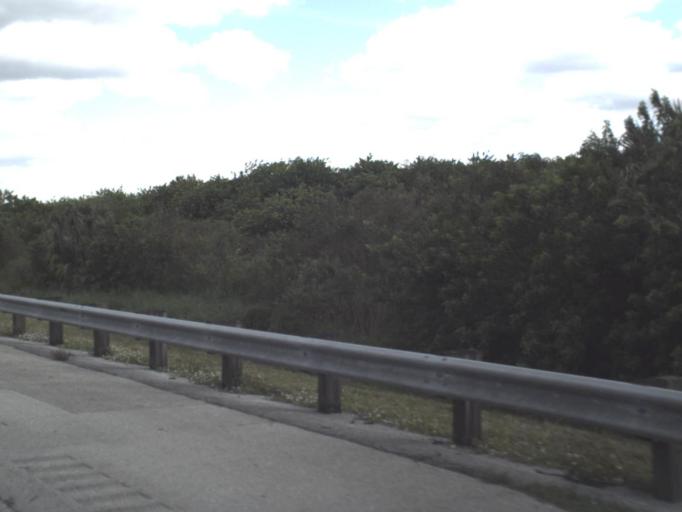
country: US
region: Florida
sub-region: Indian River County
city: Fellsmere
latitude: 27.5593
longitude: -80.7134
